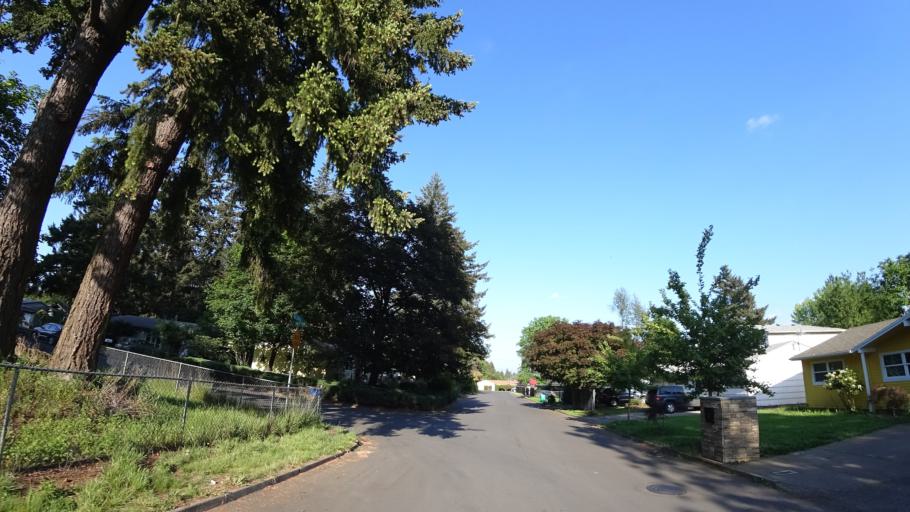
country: US
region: Oregon
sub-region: Multnomah County
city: Lents
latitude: 45.5077
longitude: -122.5122
